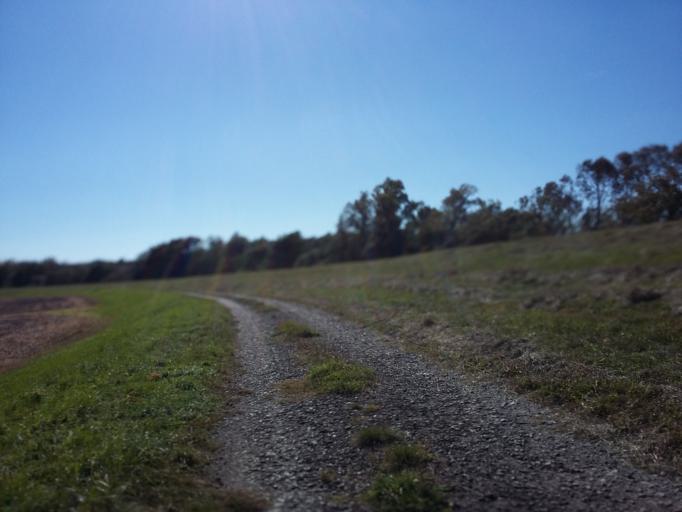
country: AT
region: Lower Austria
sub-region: Politischer Bezirk Ganserndorf
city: Marchegg
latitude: 48.3038
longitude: 16.9226
